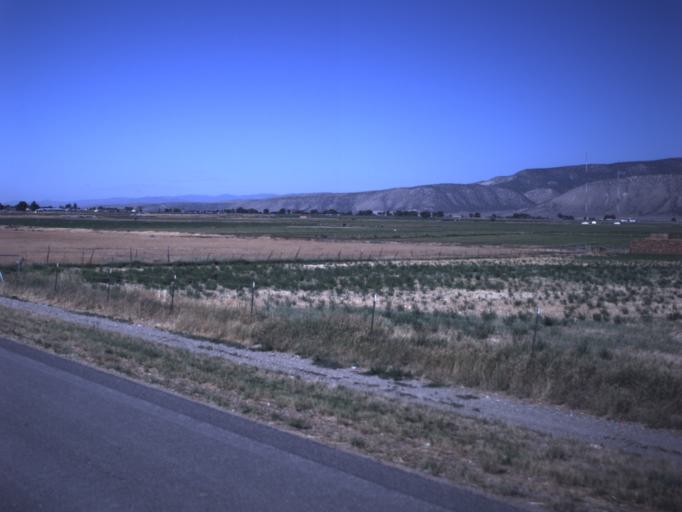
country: US
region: Utah
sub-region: Sanpete County
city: Manti
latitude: 39.2967
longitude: -111.6207
